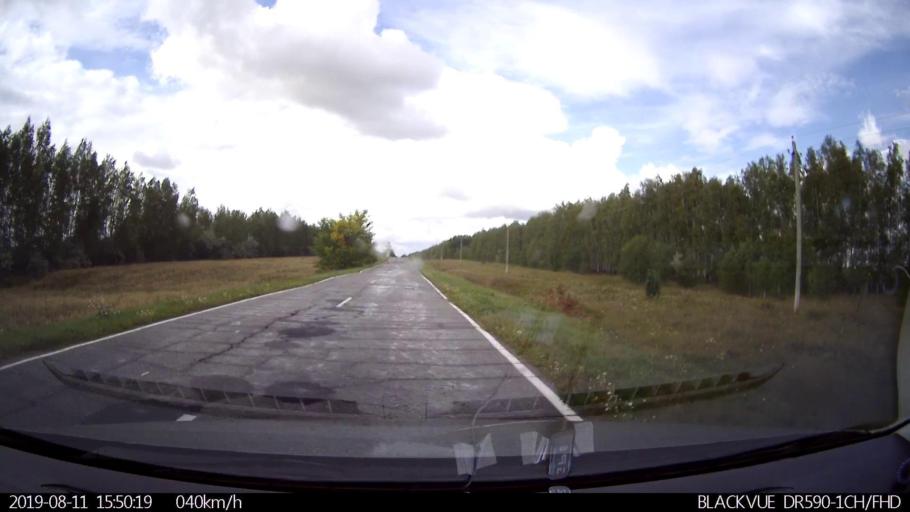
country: RU
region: Ulyanovsk
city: Ignatovka
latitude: 53.9112
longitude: 47.6558
